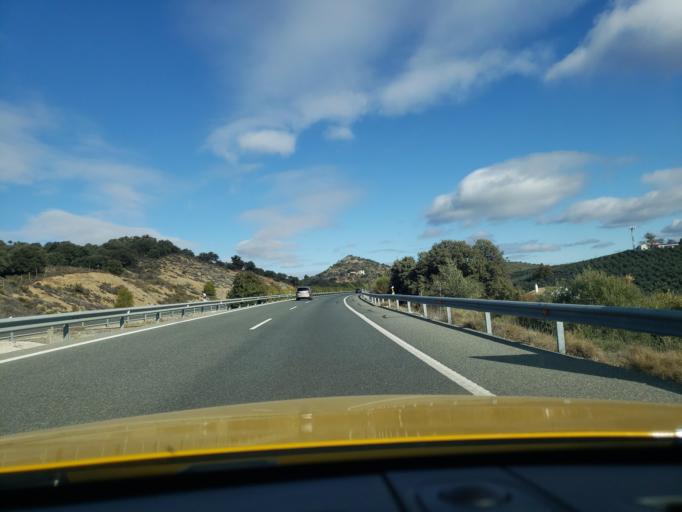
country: ES
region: Andalusia
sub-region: Provincia de Malaga
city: Villanueva del Rosario
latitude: 37.0362
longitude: -4.3890
